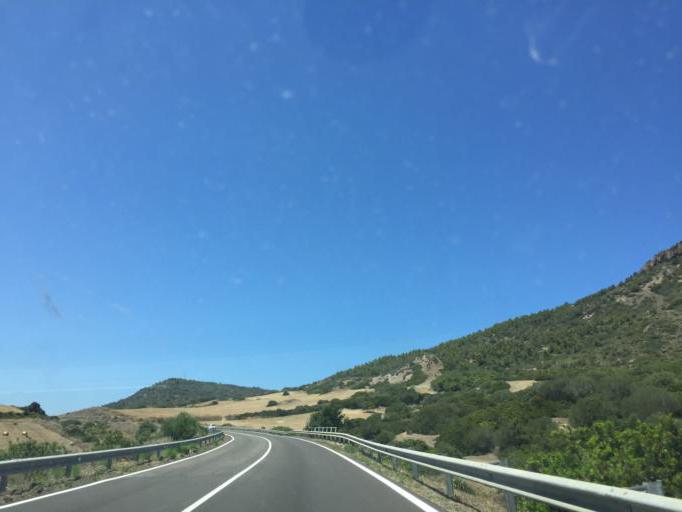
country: IT
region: Sardinia
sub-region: Provincia di Sassari
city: Valledoria
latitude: 40.9029
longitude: 8.7749
